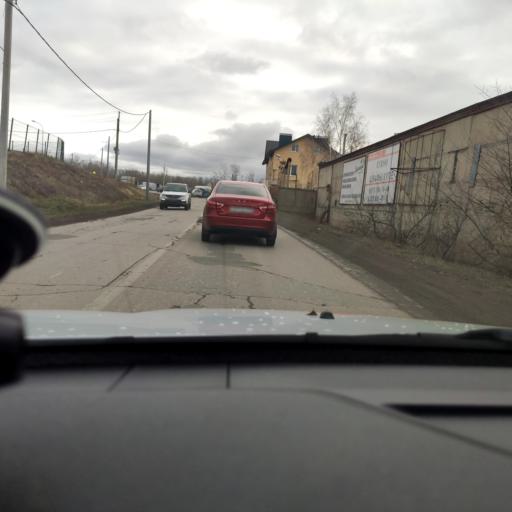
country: RU
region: Samara
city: Petra-Dubrava
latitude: 53.3013
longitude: 50.3593
